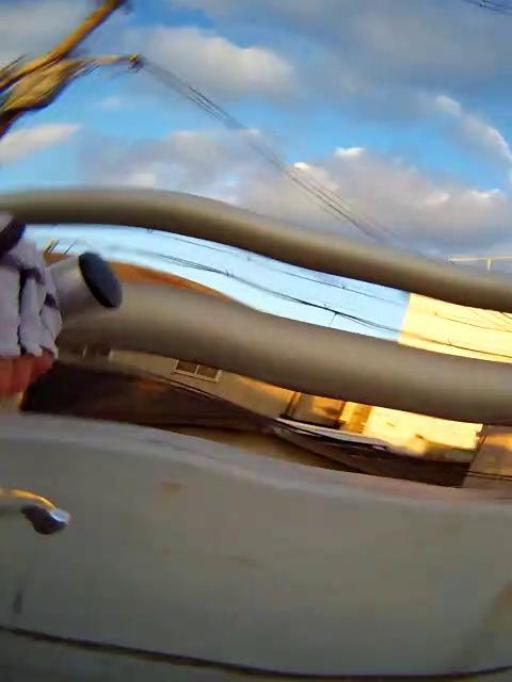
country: JP
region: Osaka
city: Osaka-shi
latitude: 34.7247
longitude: 135.4705
